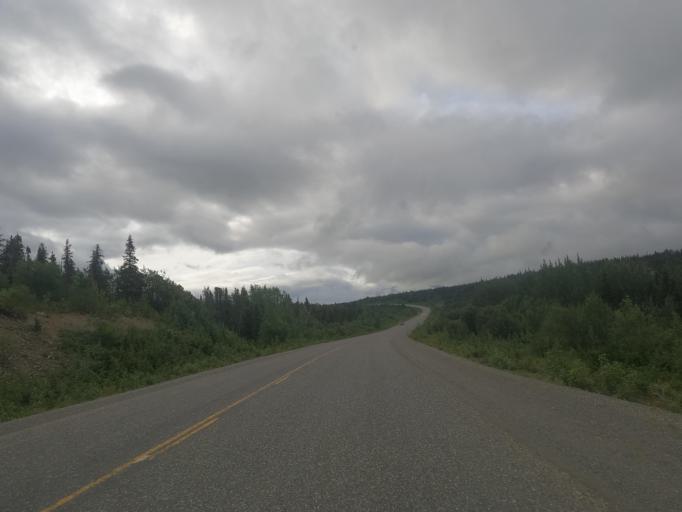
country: CA
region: Yukon
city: Haines Junction
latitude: 59.9970
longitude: -136.8456
